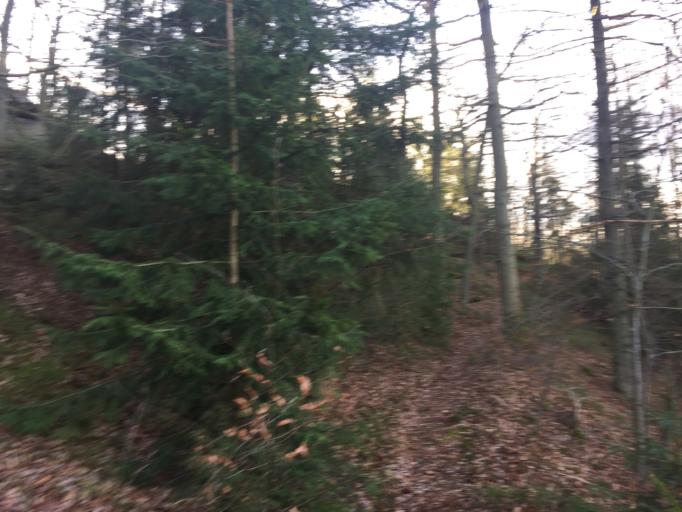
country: DE
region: Thuringia
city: Bad Blankenburg
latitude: 50.6631
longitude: 11.2538
